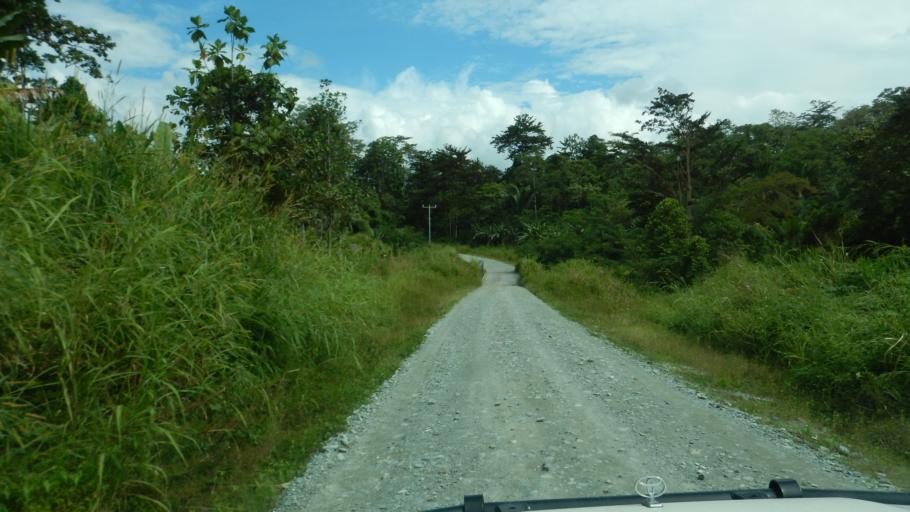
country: PG
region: Northern Province
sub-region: Sohe
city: Kokoda
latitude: -8.8906
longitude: 147.9899
